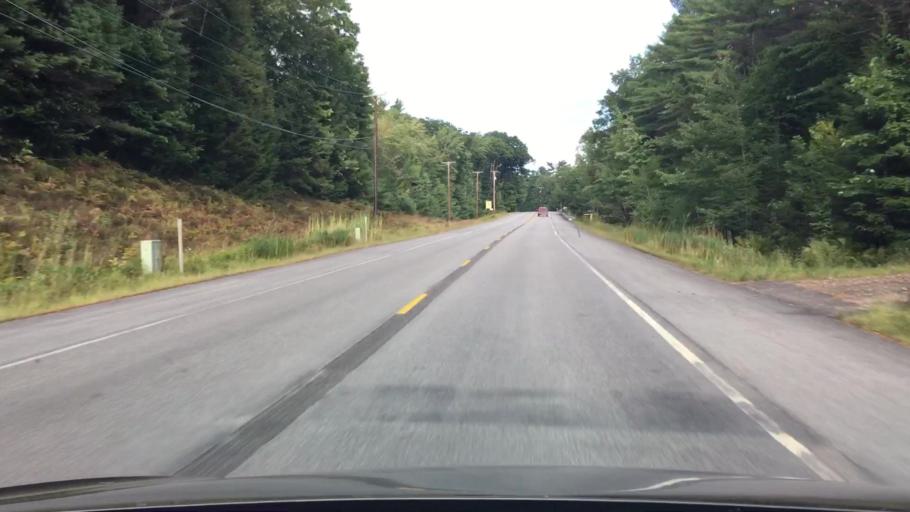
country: US
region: Maine
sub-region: Cumberland County
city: Bridgton
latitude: 44.0678
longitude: -70.7893
